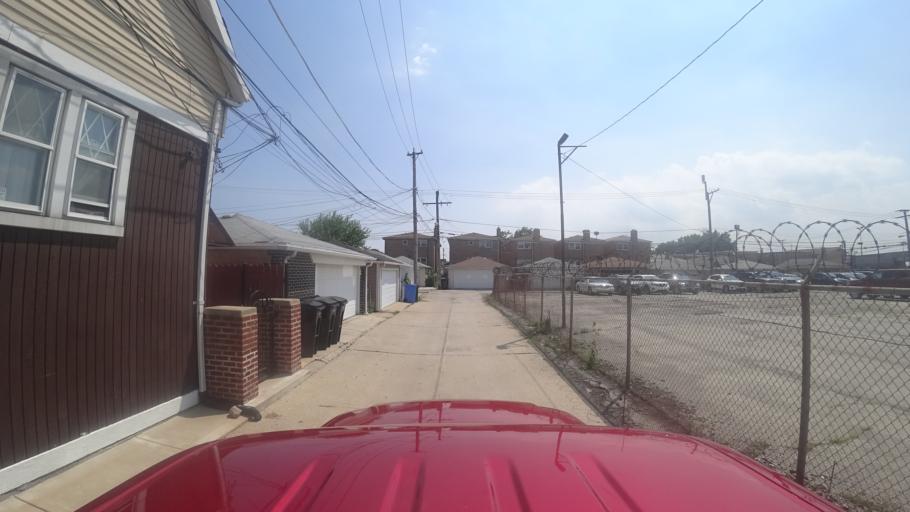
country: US
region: Illinois
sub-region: Cook County
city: Stickney
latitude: 41.7939
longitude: -87.7361
